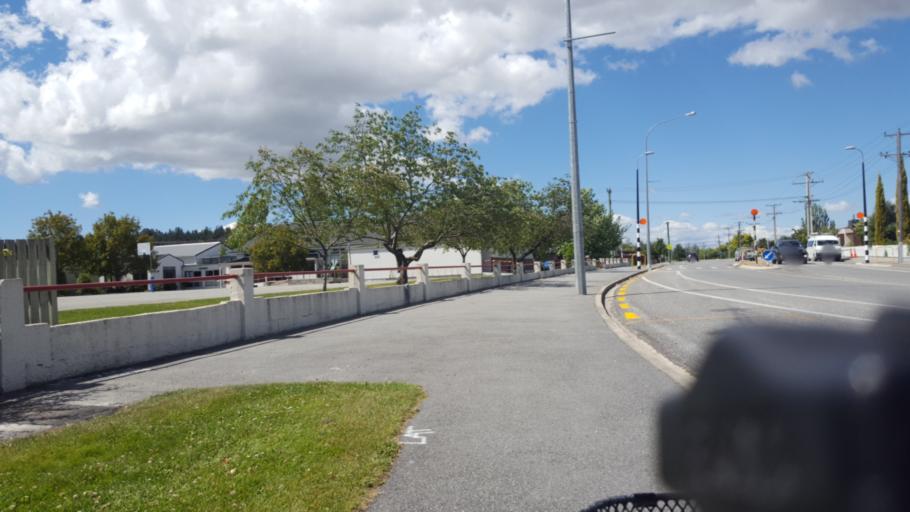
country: NZ
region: Otago
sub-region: Queenstown-Lakes District
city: Wanaka
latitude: -45.2500
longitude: 169.3965
